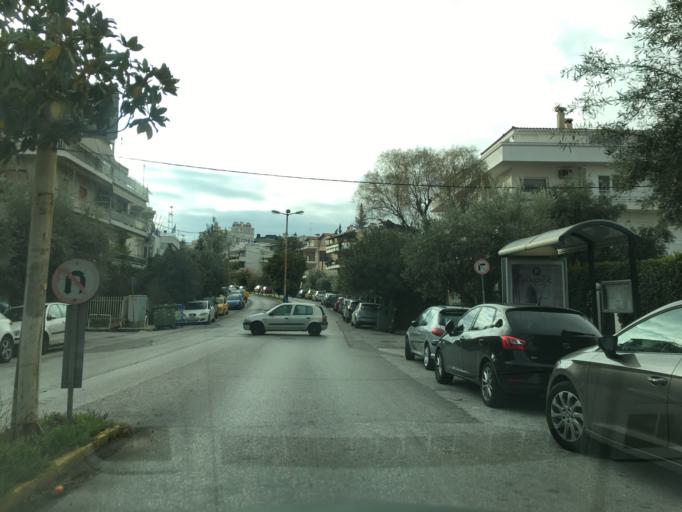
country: GR
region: Attica
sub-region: Nomarchia Athinas
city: Filothei
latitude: 38.0290
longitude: 23.7856
